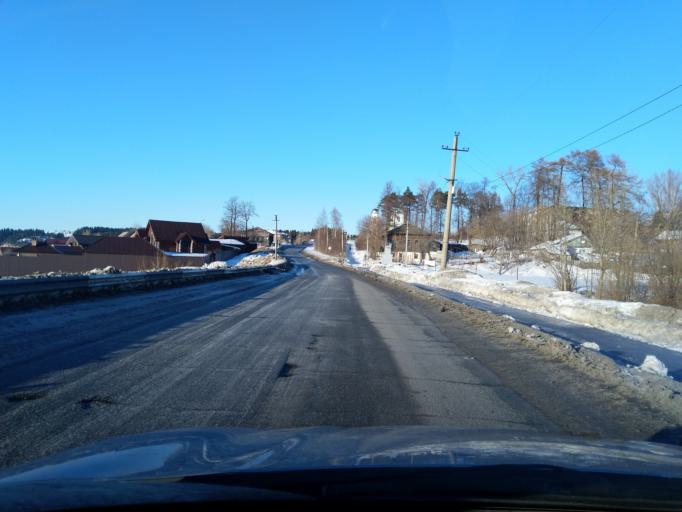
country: RU
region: Perm
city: Polazna
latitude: 58.3050
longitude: 56.4191
